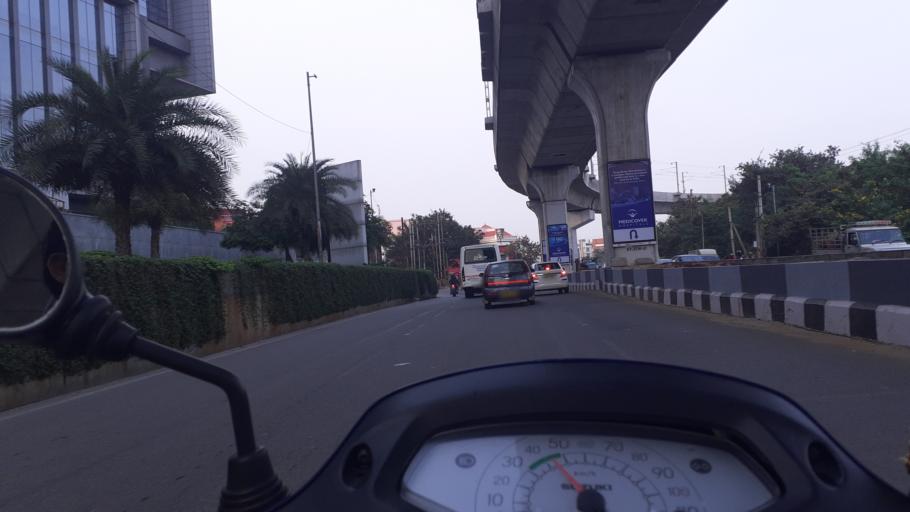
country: IN
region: Telangana
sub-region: Rangareddi
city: Kukatpalli
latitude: 17.4494
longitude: 78.3784
